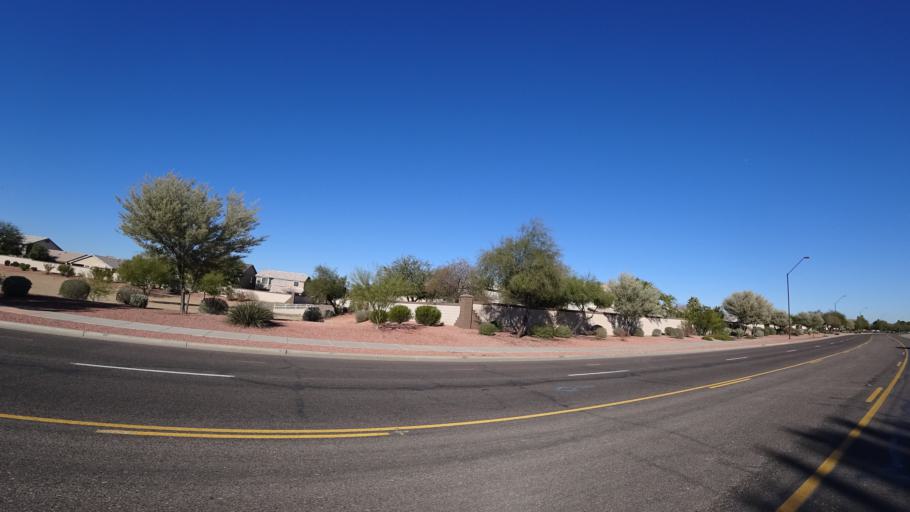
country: US
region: Arizona
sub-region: Maricopa County
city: Tolleson
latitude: 33.4208
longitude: -112.3008
